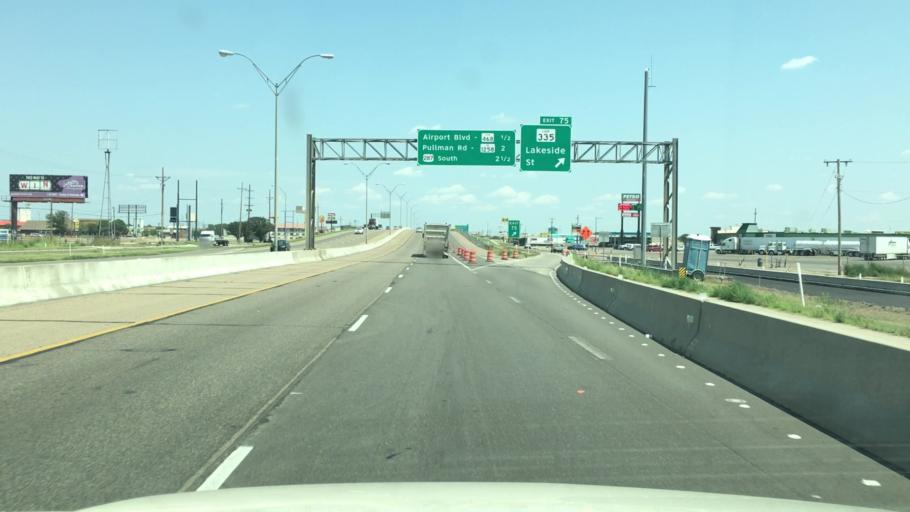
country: US
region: Texas
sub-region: Potter County
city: Amarillo
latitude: 35.1926
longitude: -101.7466
